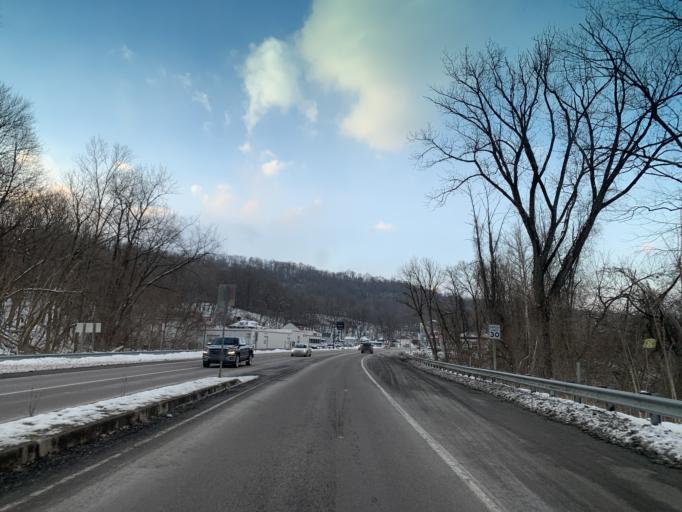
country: US
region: Maryland
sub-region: Allegany County
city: La Vale
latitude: 39.6707
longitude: -78.7907
